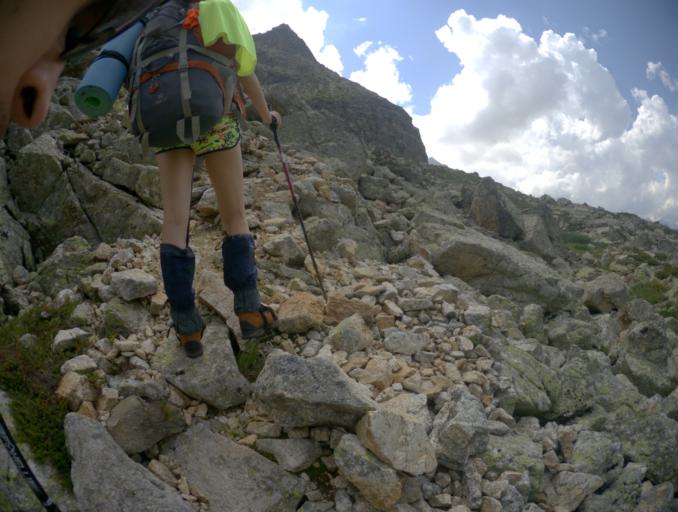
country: RU
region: Karachayevo-Cherkesiya
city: Uchkulan
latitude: 43.2881
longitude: 42.0814
